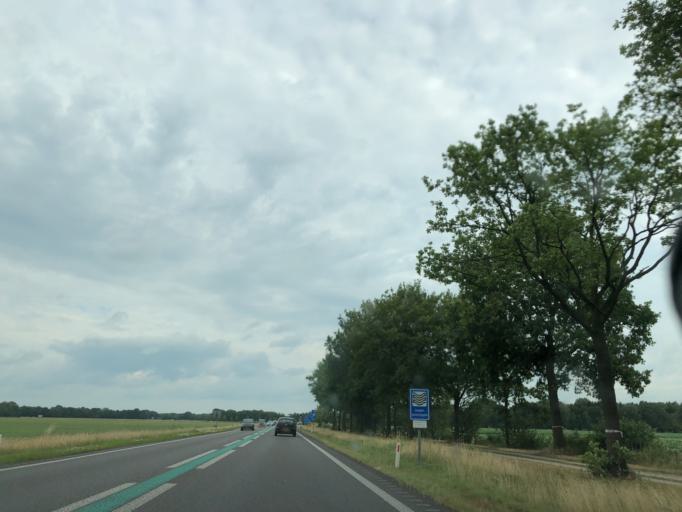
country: NL
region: Drenthe
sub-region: Gemeente Borger-Odoorn
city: Borger
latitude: 52.9807
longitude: 6.7722
